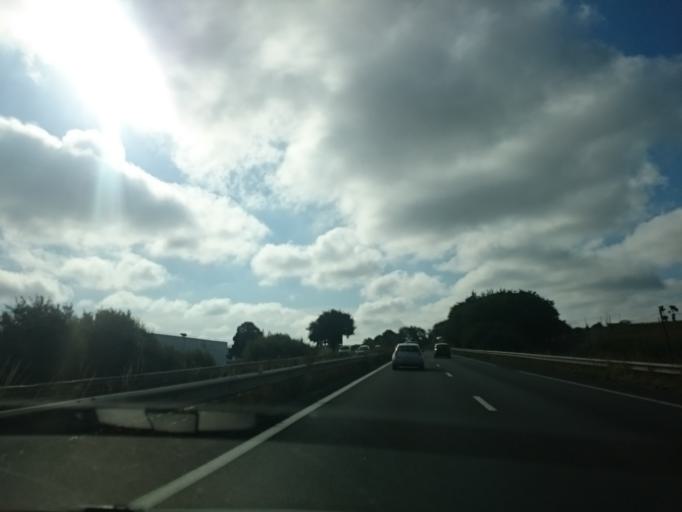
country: FR
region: Brittany
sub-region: Departement des Cotes-d'Armor
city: Lamballe
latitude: 48.4622
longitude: -2.5407
